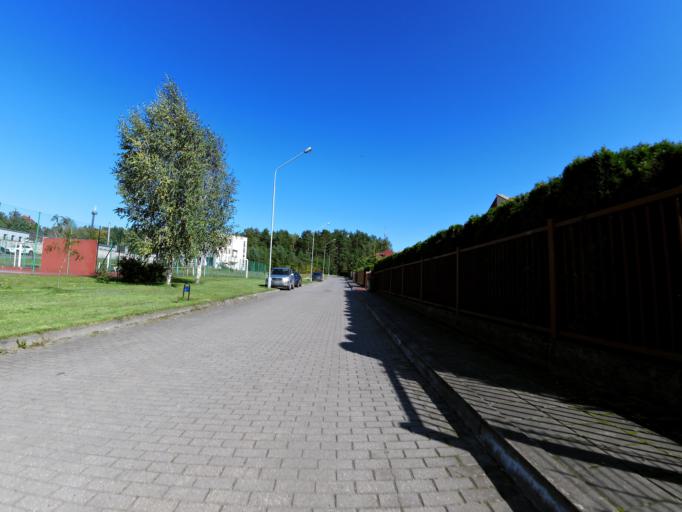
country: LT
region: Vilnius County
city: Lazdynai
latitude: 54.6752
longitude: 25.1901
